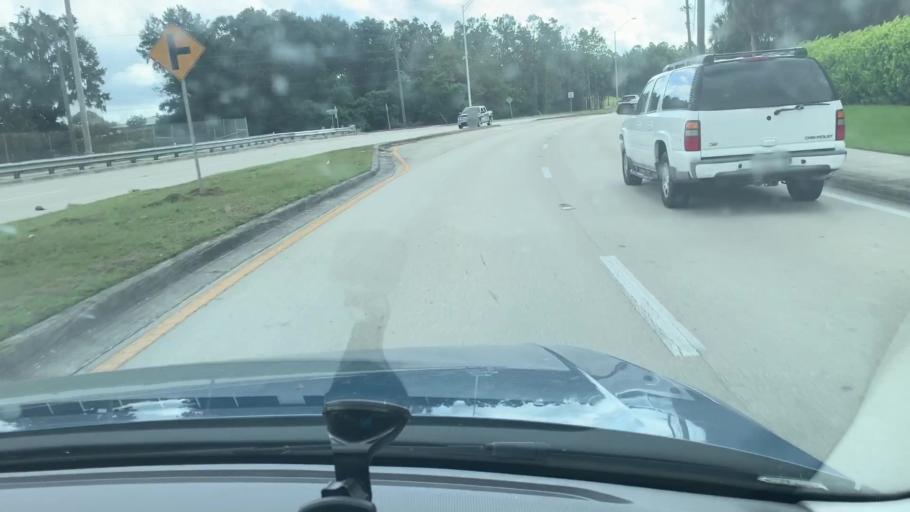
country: US
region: Florida
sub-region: Polk County
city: Gibsonia
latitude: 28.0956
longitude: -81.9991
